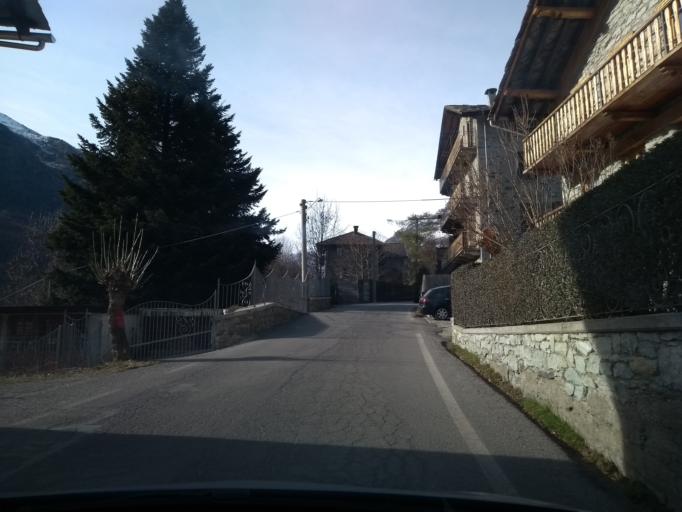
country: IT
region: Piedmont
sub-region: Provincia di Torino
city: Ala di Stura
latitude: 45.3153
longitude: 7.2980
